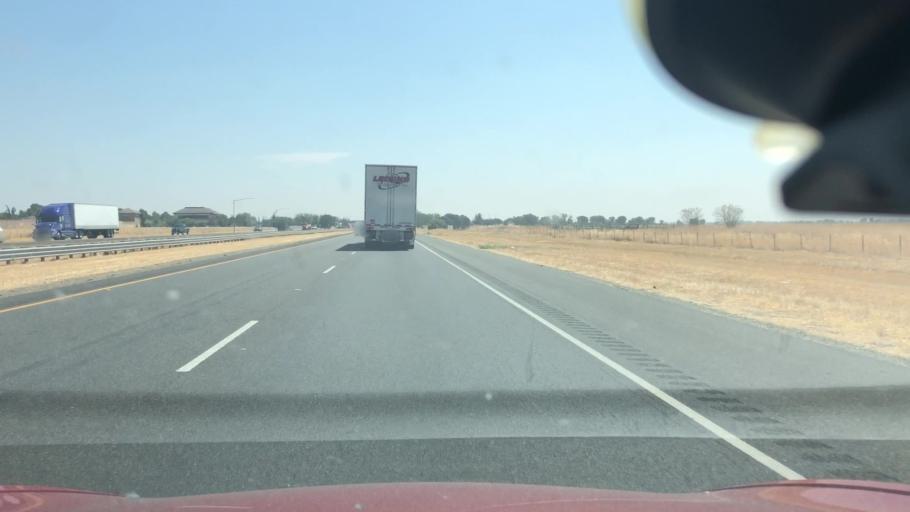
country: US
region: California
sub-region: Sacramento County
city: Laguna
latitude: 38.4172
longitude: -121.4858
